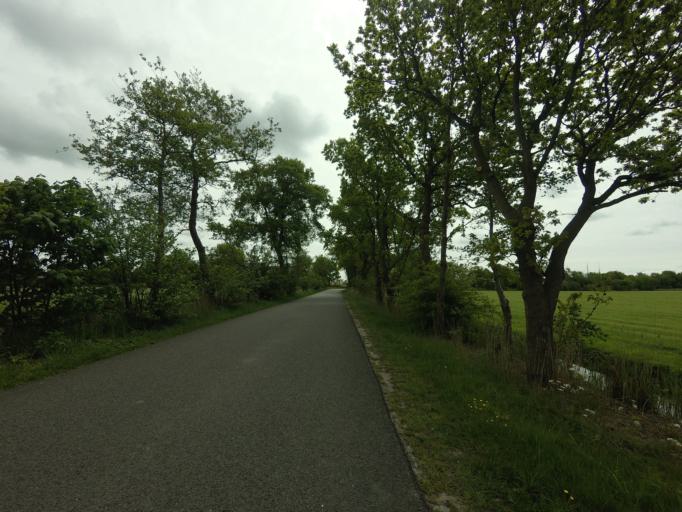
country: NL
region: Friesland
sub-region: Sudwest Fryslan
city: Koudum
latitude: 52.9046
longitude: 5.4634
